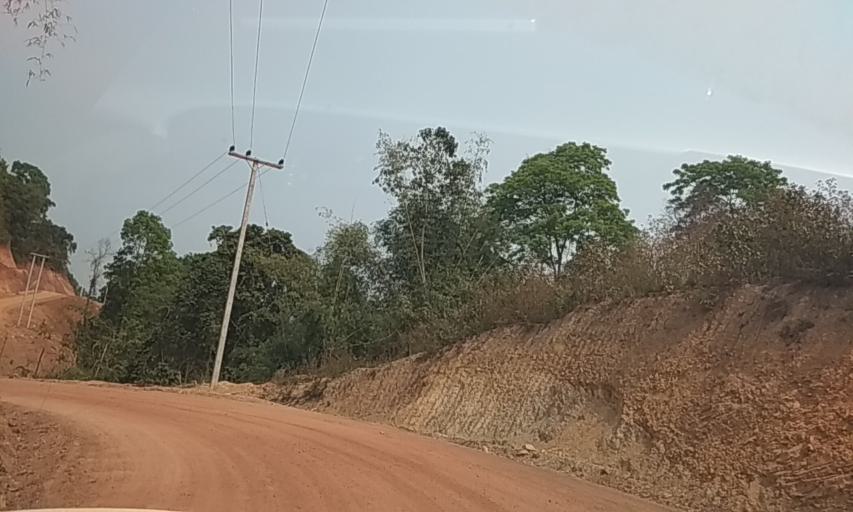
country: VN
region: Huyen Dien Bien
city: Dien Bien Phu
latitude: 21.4584
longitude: 102.7731
